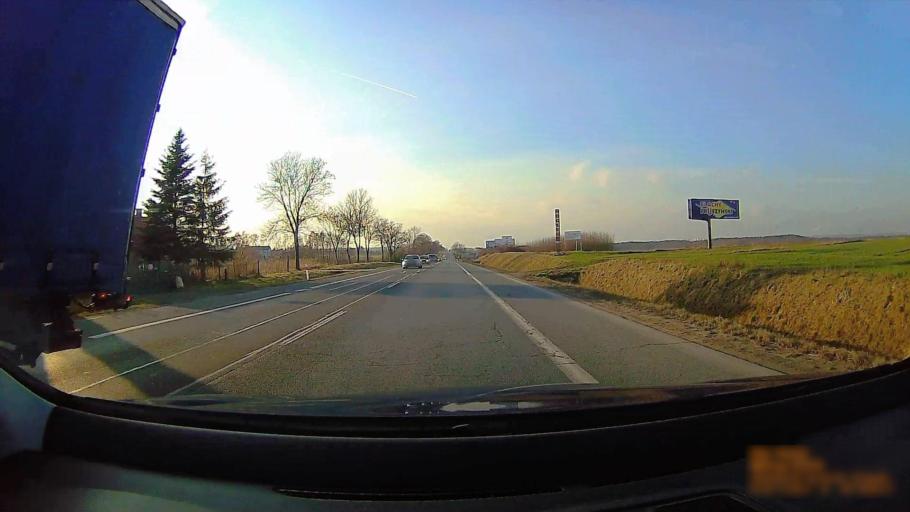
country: PL
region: Greater Poland Voivodeship
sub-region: Konin
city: Konin
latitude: 52.1916
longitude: 18.3281
